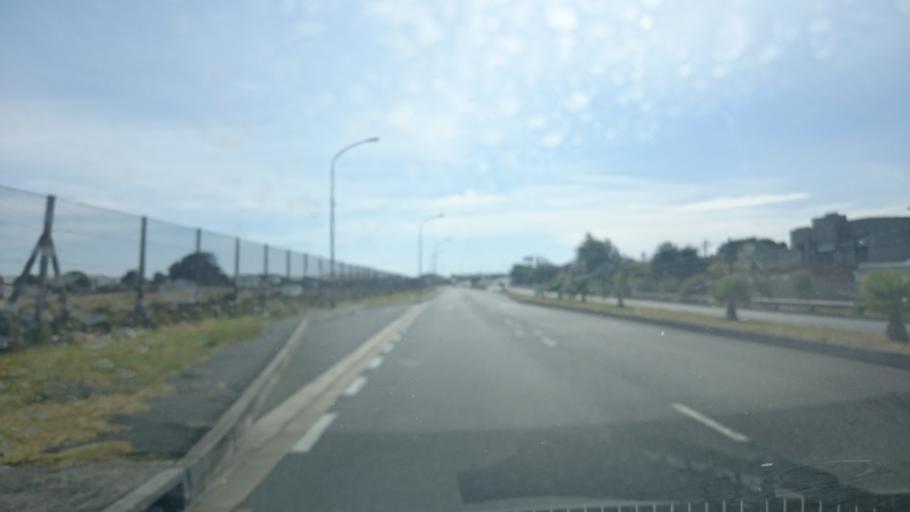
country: ZA
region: Western Cape
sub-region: City of Cape Town
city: Lansdowne
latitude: -34.0125
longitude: 18.4903
